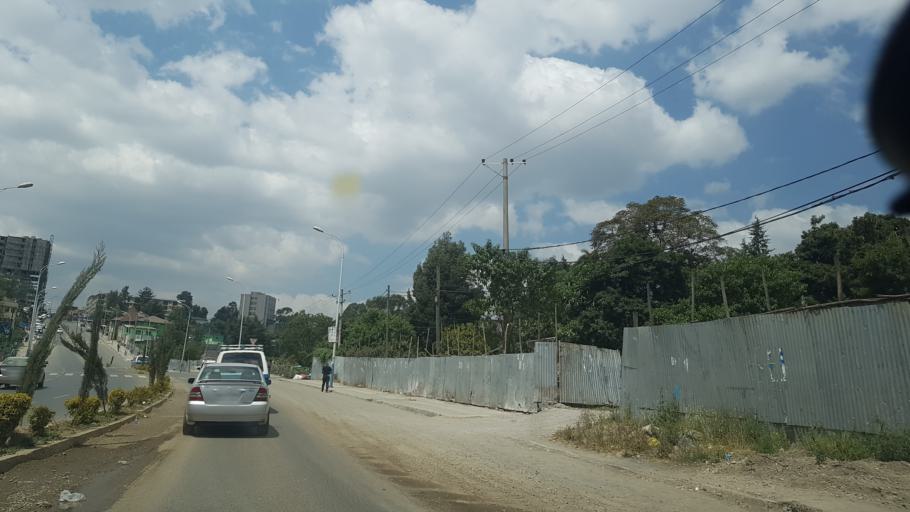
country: ET
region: Adis Abeba
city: Addis Ababa
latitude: 9.0278
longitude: 38.7500
